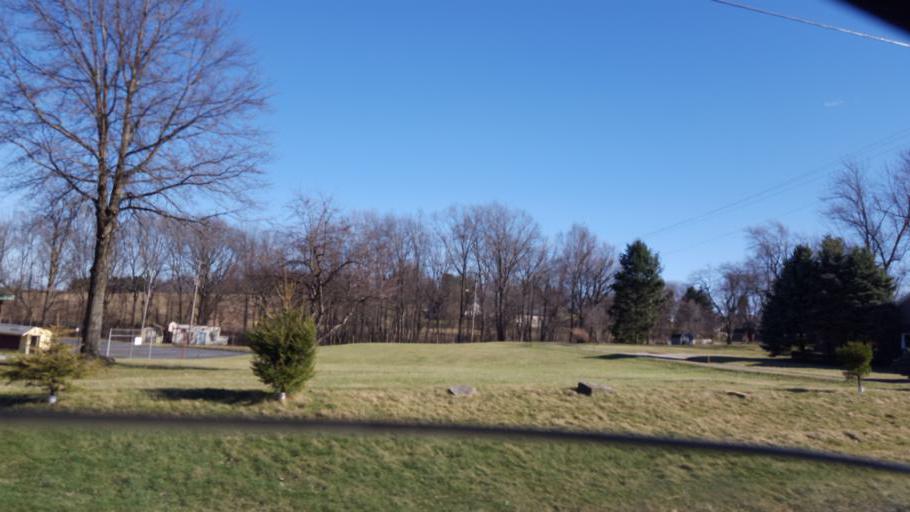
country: US
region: Ohio
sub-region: Wayne County
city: Dalton
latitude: 40.6972
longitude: -81.7012
